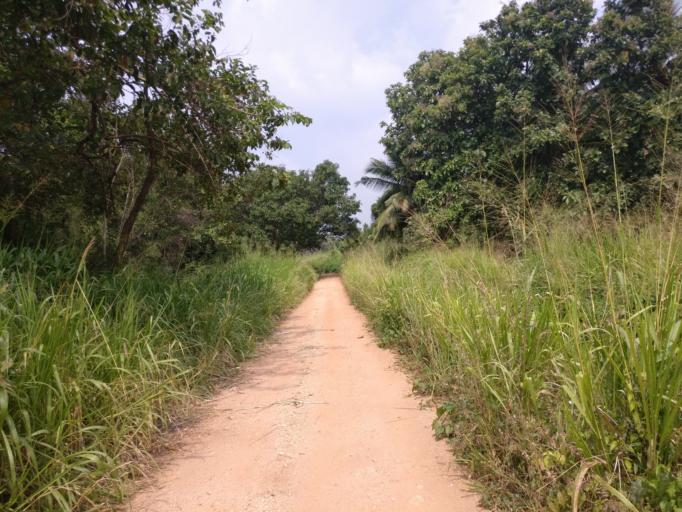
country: LK
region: Central
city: Dambulla
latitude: 7.8381
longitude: 80.6522
